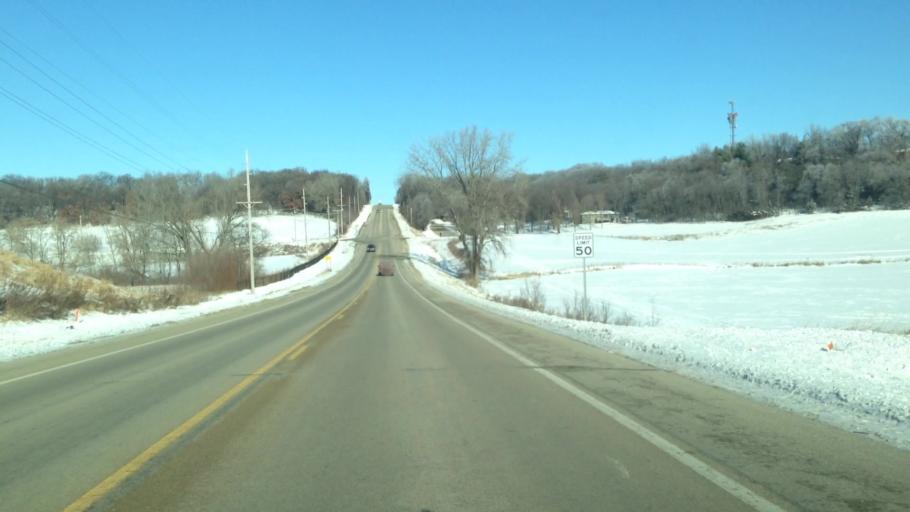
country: US
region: Minnesota
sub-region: Olmsted County
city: Rochester
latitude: 44.0851
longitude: -92.4887
